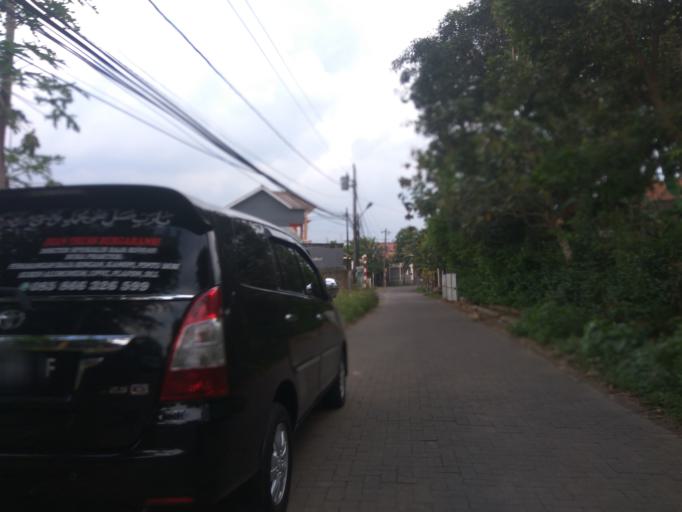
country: ID
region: Central Java
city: Semarang
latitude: -7.0639
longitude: 110.4466
